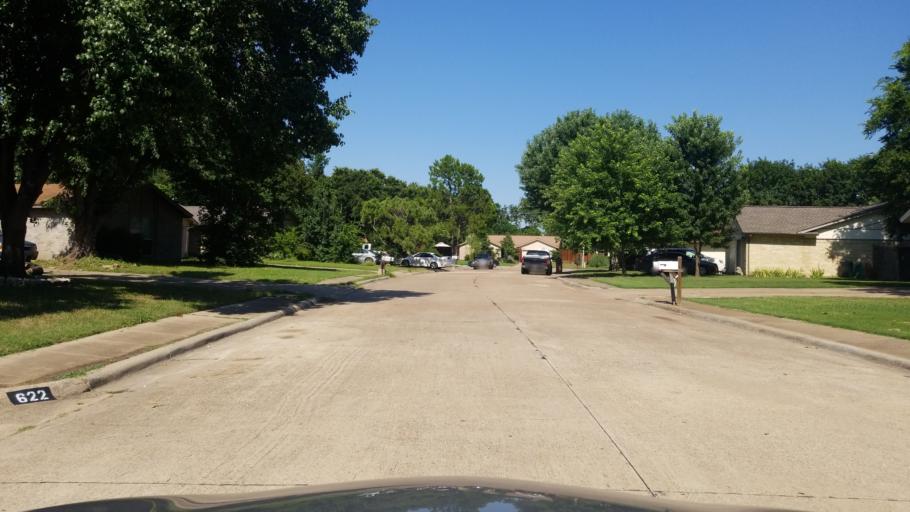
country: US
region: Texas
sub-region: Dallas County
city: Grand Prairie
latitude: 32.6794
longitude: -97.0124
